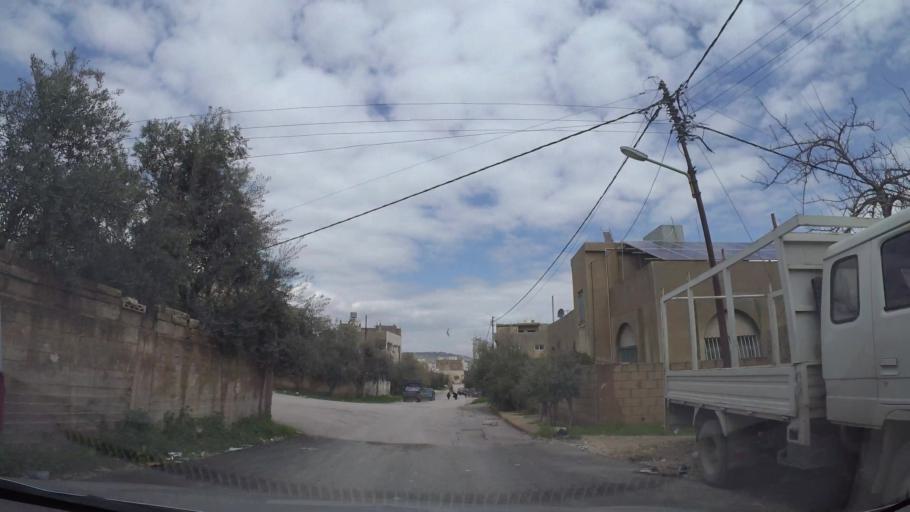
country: JO
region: Amman
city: Al Jubayhah
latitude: 32.0600
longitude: 35.8289
